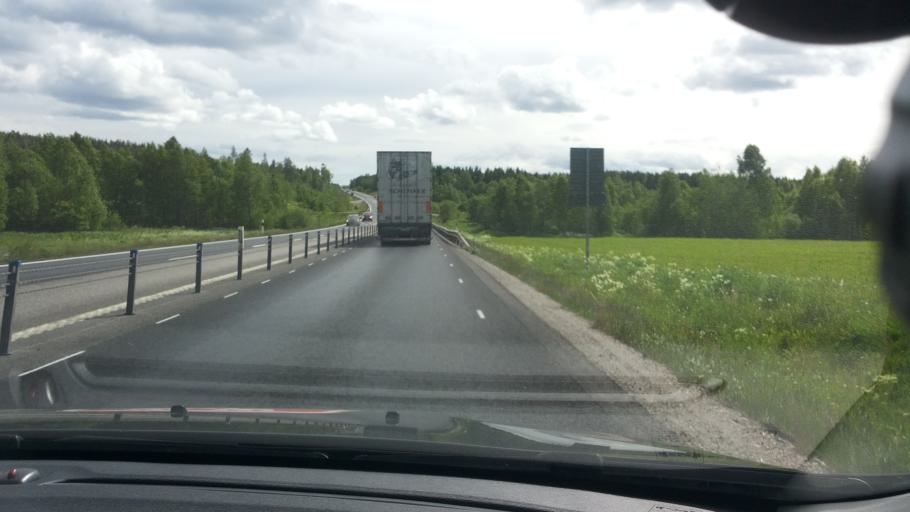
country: SE
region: Vaesternorrland
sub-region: Sundsvalls Kommun
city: Njurundabommen
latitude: 62.2260
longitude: 17.3718
